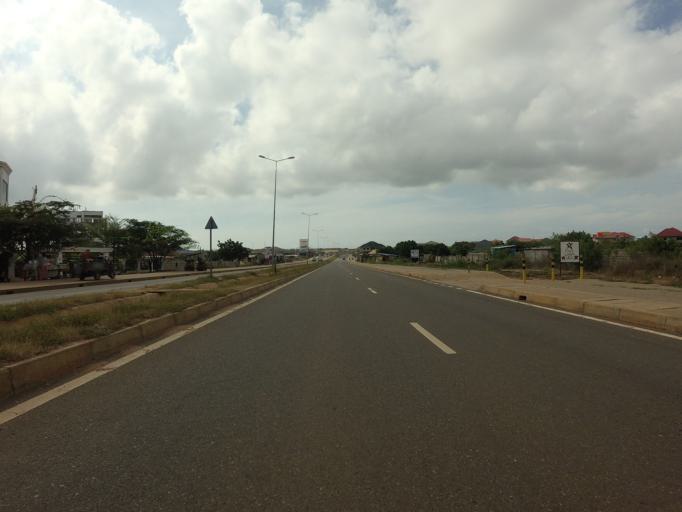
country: GH
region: Greater Accra
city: Teshi Old Town
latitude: 5.5989
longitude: -0.1360
